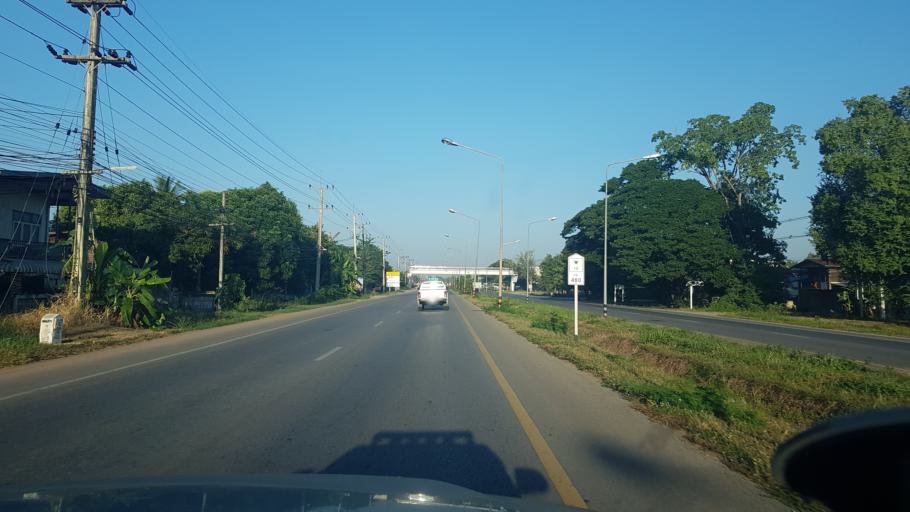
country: TH
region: Chaiyaphum
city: Khon San
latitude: 16.5864
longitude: 102.0054
